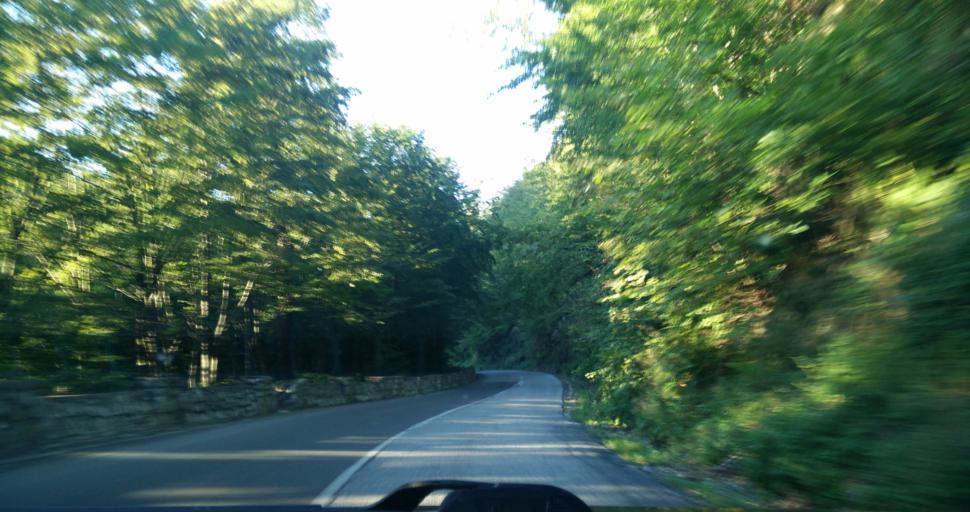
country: RO
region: Bihor
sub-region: Oras Nucet
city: Nucet
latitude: 46.4827
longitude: 22.5973
